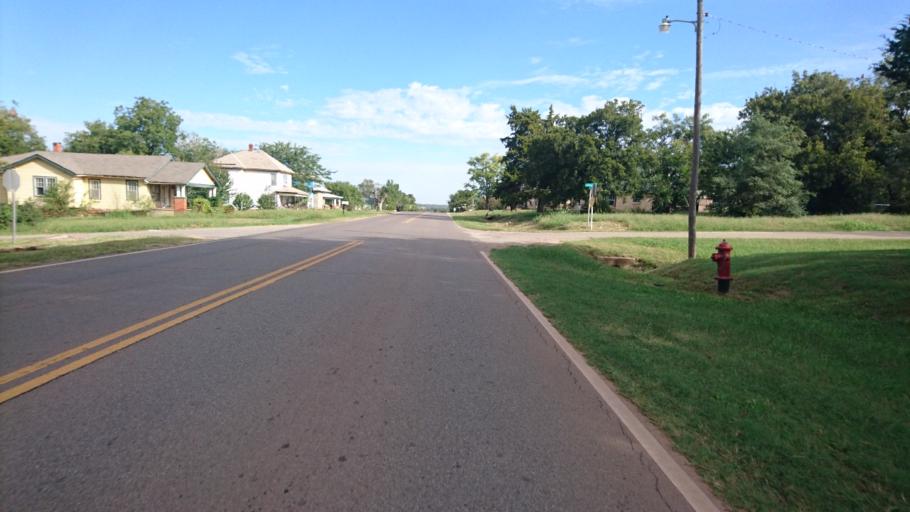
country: US
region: Oklahoma
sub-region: Oklahoma County
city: Luther
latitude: 35.6912
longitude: -97.0625
